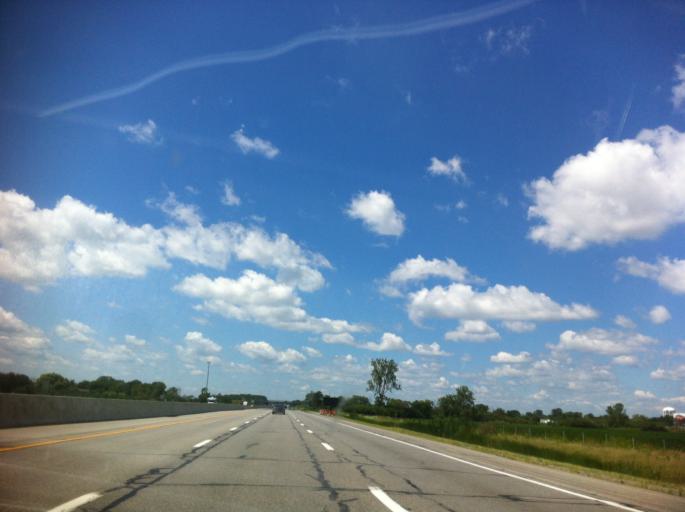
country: US
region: Ohio
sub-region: Wood County
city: Walbridge
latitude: 41.5449
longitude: -83.5289
